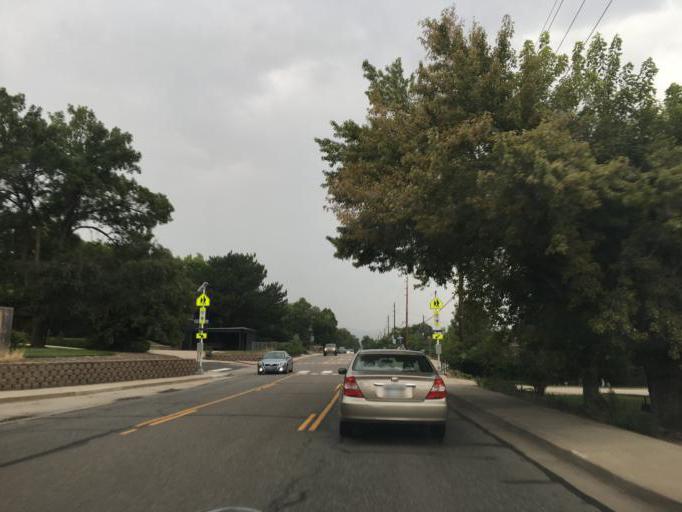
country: US
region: Colorado
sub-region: Jefferson County
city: Wheat Ridge
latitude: 39.7693
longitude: -105.1013
